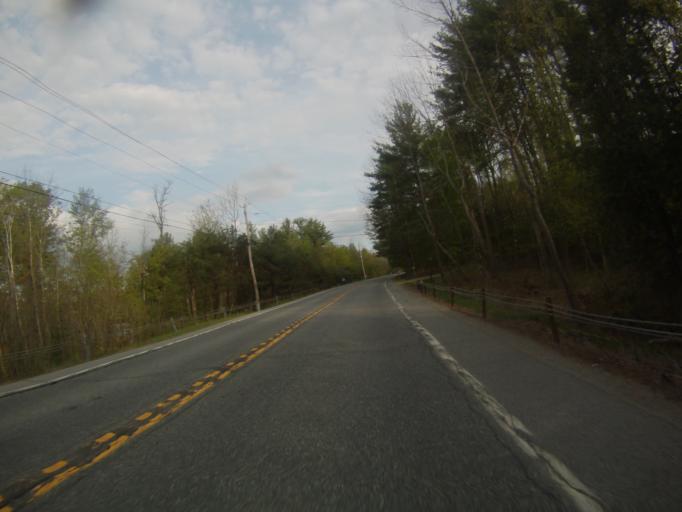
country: US
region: New York
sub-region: Warren County
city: Warrensburg
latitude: 43.6586
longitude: -73.9522
